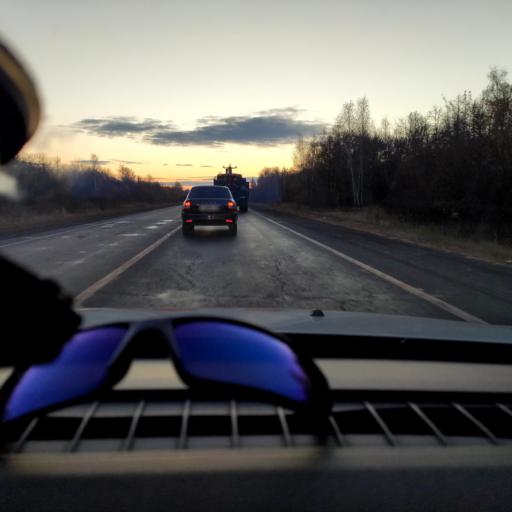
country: RU
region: Samara
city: Chapayevsk
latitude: 52.9936
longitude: 49.8232
